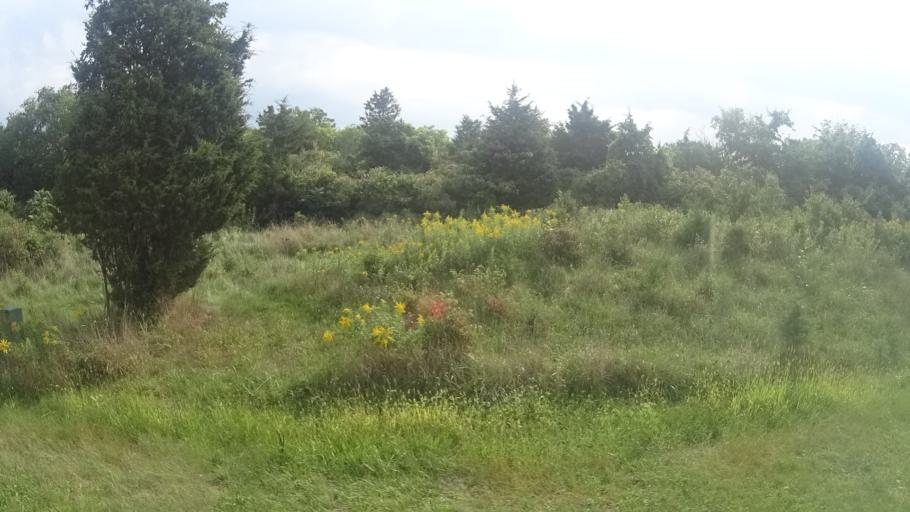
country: US
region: Ohio
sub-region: Erie County
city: Sandusky
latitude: 41.5942
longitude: -82.6960
